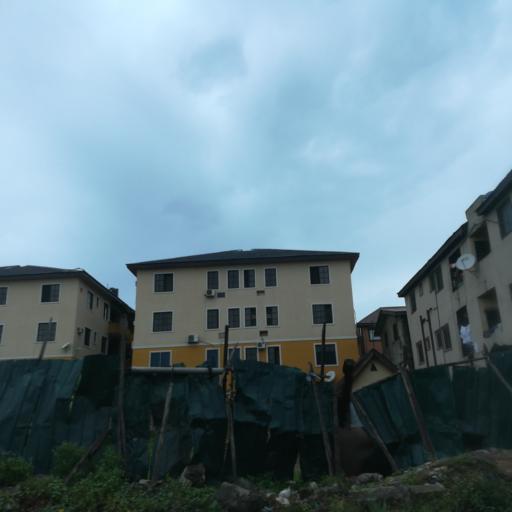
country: NG
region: Lagos
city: Ebute Metta
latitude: 6.4874
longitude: 3.3838
